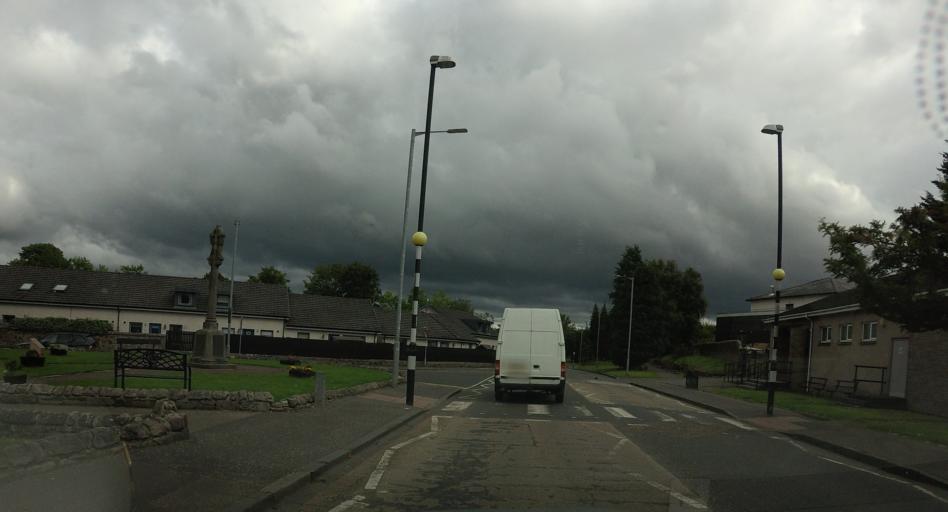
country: GB
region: Scotland
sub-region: Clackmannanshire
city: Alloa
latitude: 56.1260
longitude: -3.7840
